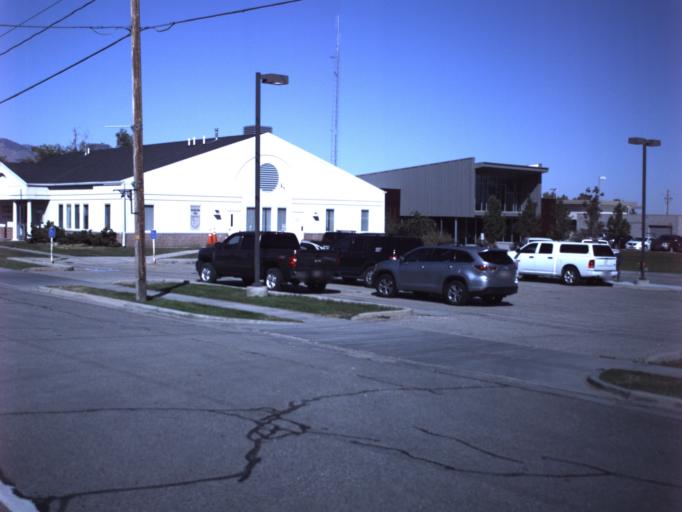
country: US
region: Utah
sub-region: Tooele County
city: Grantsville
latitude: 40.5998
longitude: -112.4456
